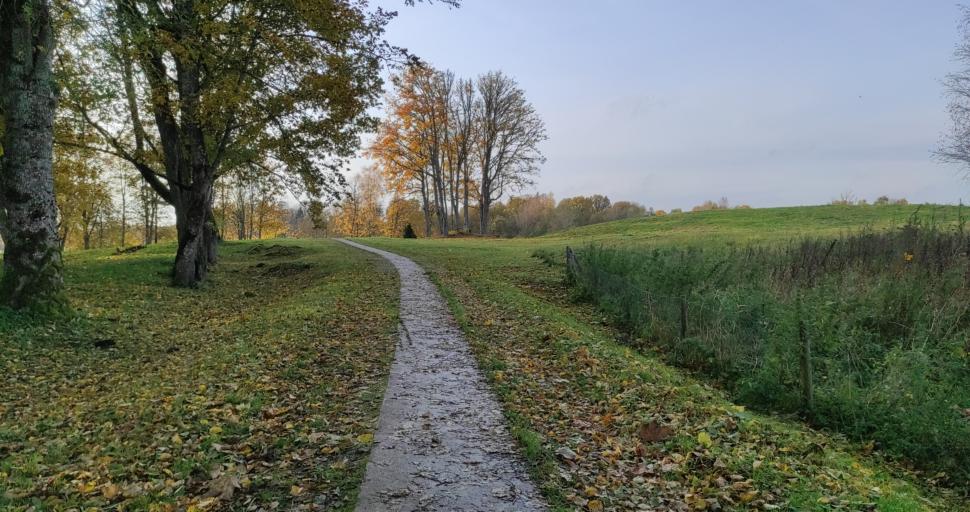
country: LV
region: Vainode
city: Vainode
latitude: 56.4445
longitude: 21.8585
